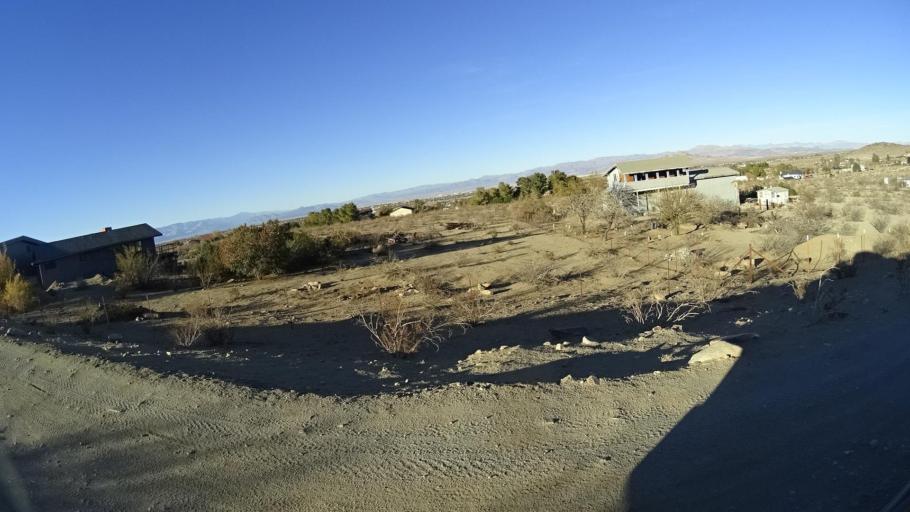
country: US
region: California
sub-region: Kern County
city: Ridgecrest
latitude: 35.5785
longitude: -117.6605
